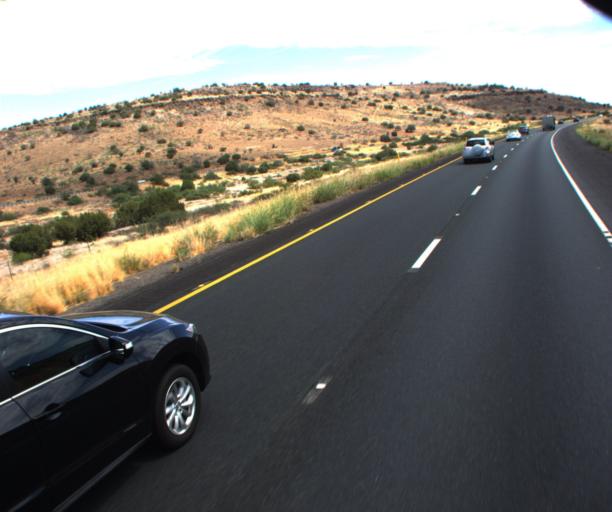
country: US
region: Arizona
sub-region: Yavapai County
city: Camp Verde
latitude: 34.4791
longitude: -112.0195
